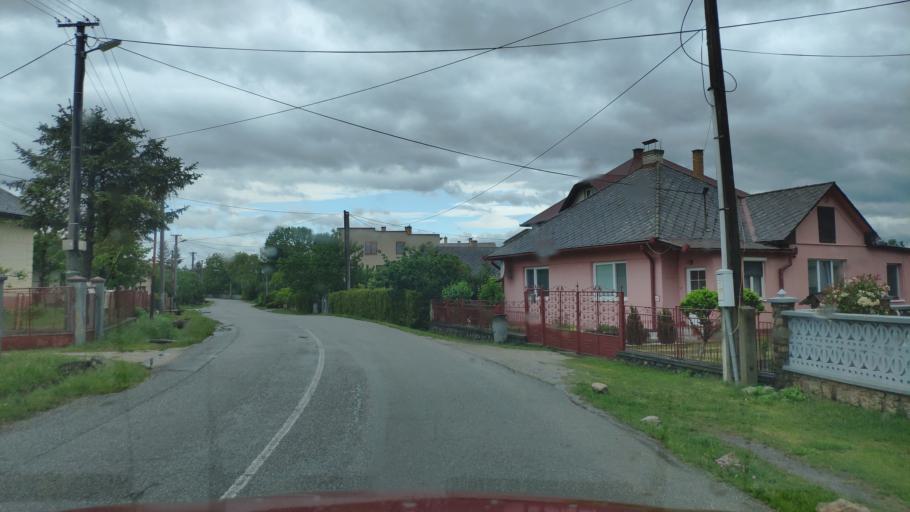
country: SK
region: Kosicky
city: Moldava nad Bodvou
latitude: 48.5434
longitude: 21.0465
